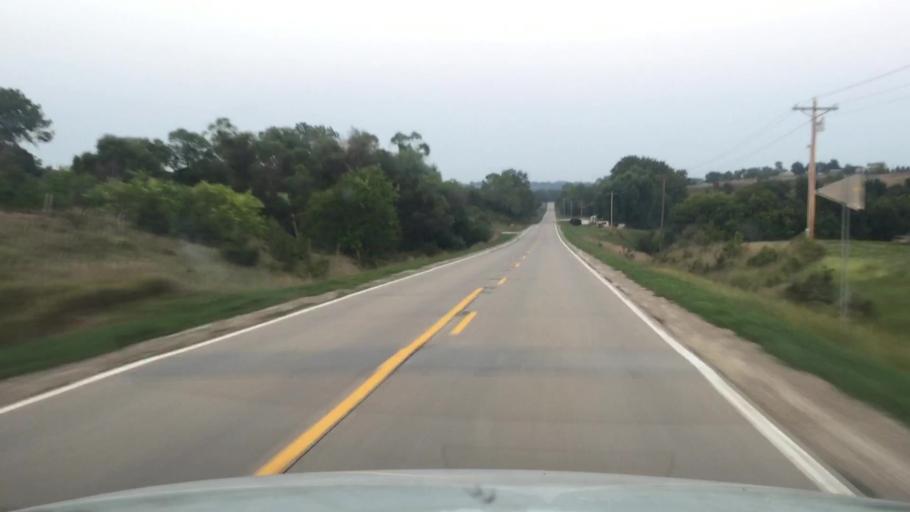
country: US
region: Iowa
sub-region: Warren County
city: Indianola
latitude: 41.1909
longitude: -93.6510
